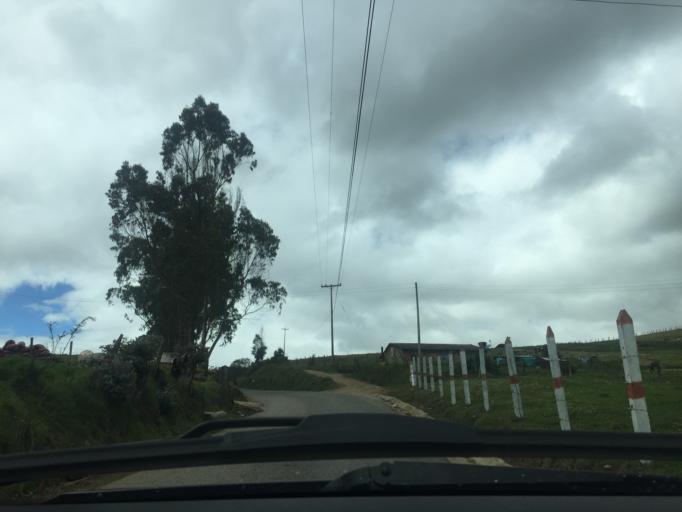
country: CO
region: Cundinamarca
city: Villapinzon
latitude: 5.2162
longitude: -73.6233
